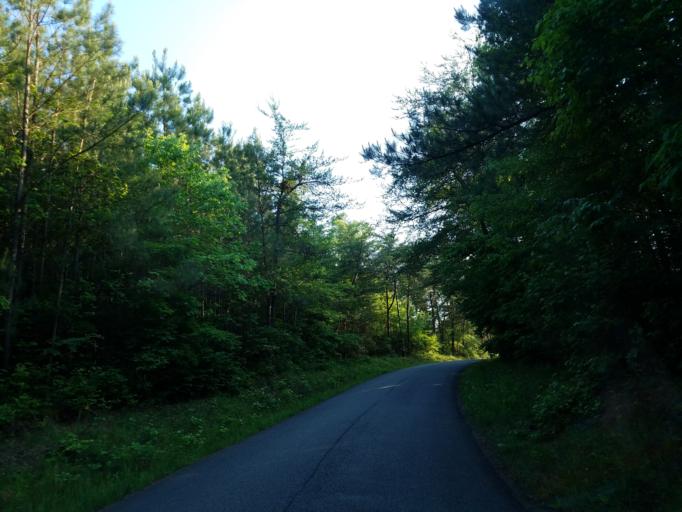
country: US
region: Georgia
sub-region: Cherokee County
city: Ball Ground
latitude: 34.3370
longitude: -84.3346
